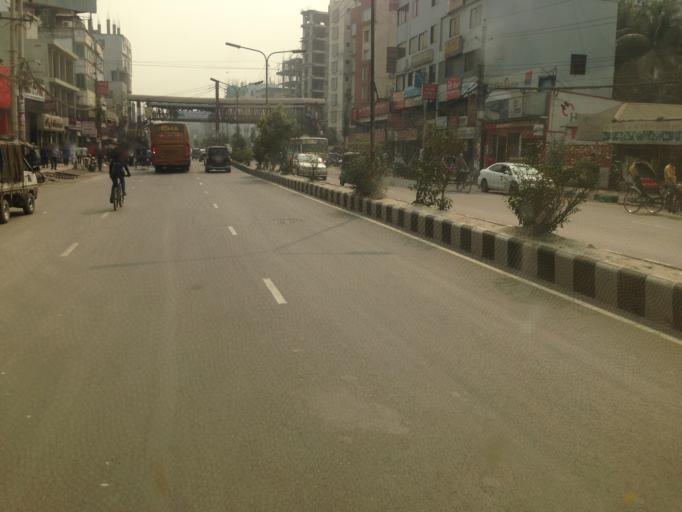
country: BD
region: Dhaka
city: Paltan
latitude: 23.8104
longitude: 90.4213
